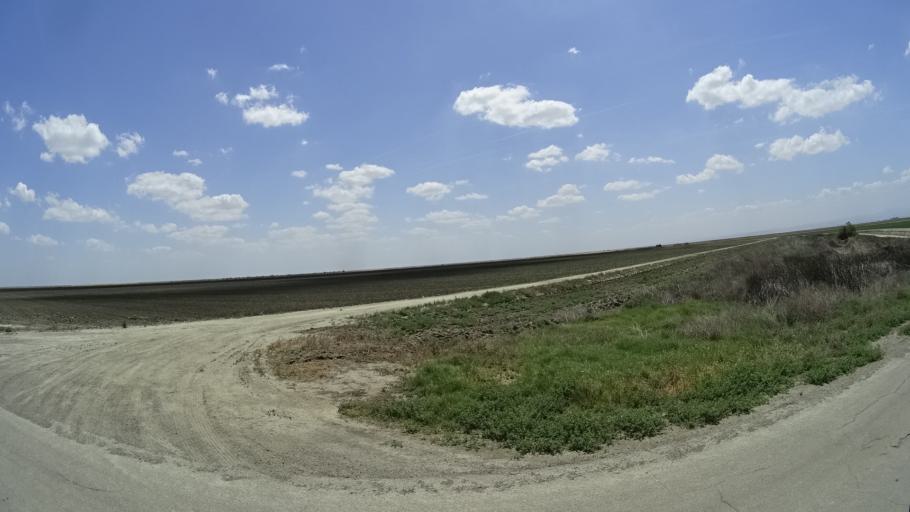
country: US
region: California
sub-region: Kings County
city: Stratford
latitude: 36.1527
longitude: -119.8202
